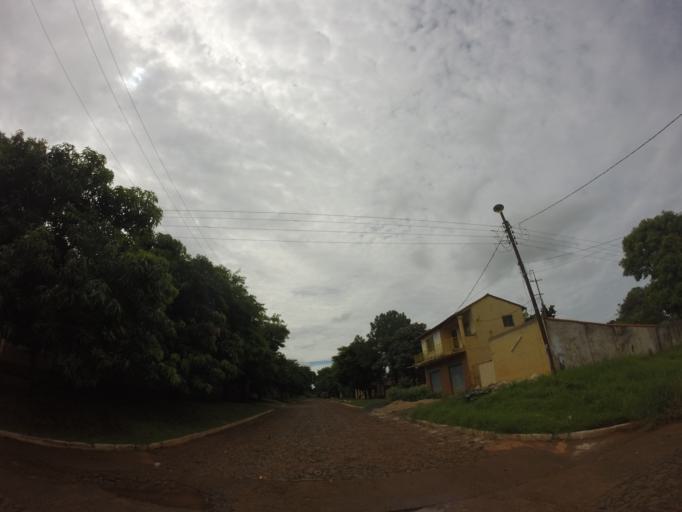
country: PY
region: Alto Parana
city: Ciudad del Este
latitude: -25.4057
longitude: -54.6499
